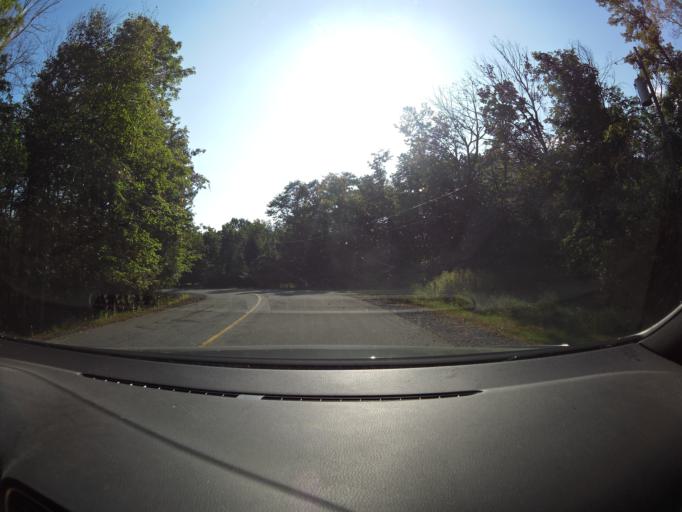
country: CA
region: Ontario
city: Arnprior
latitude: 45.4631
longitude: -76.2868
